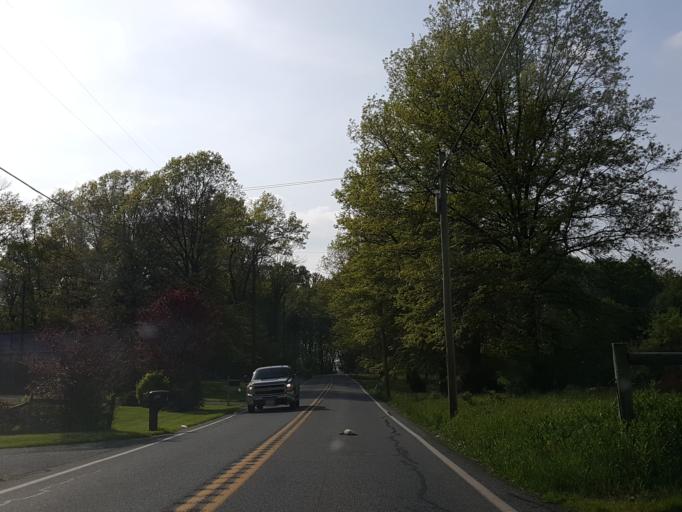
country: US
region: Pennsylvania
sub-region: Lebanon County
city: Campbelltown
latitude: 40.2462
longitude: -76.6005
